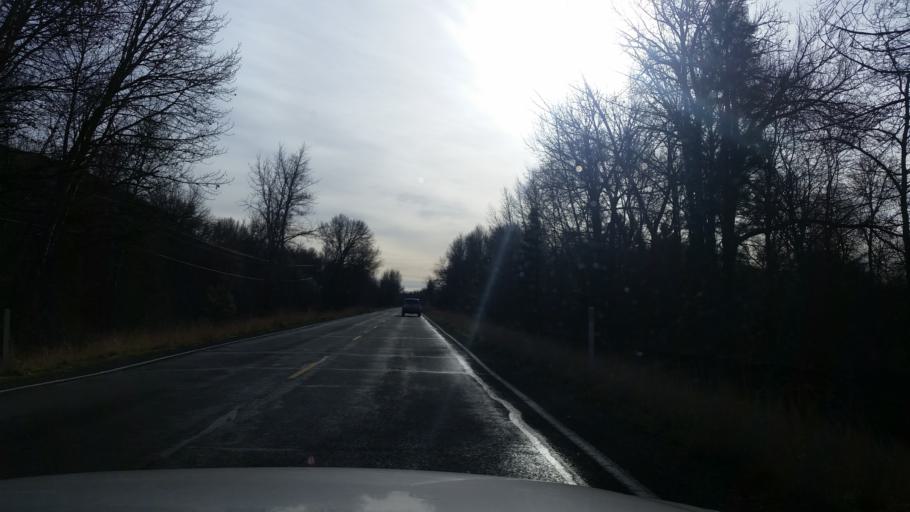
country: US
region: Washington
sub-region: Kittitas County
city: Ellensburg
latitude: 47.0639
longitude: -120.6504
